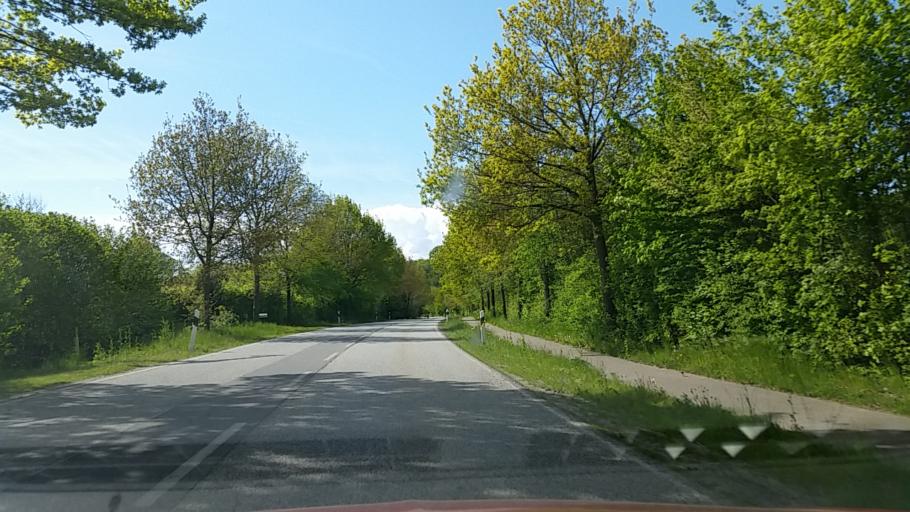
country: DE
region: Schleswig-Holstein
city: Meddewade
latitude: 53.8203
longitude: 10.4533
